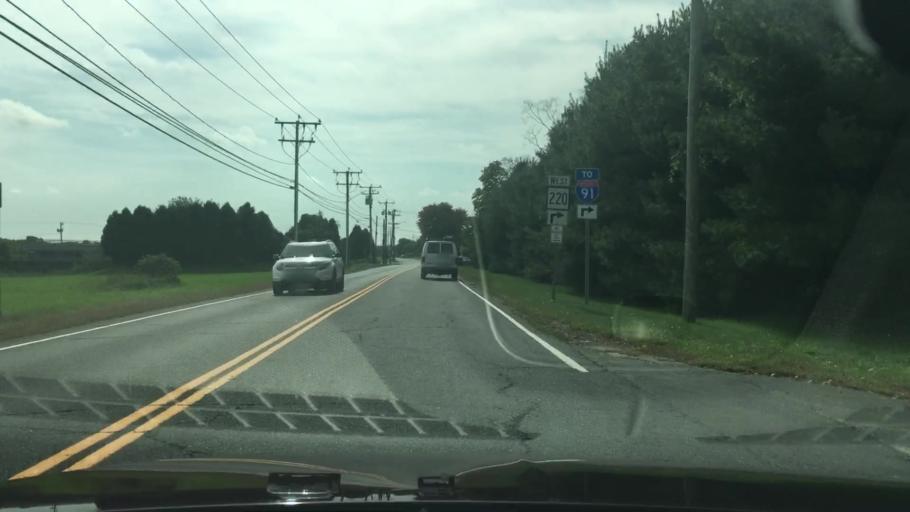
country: US
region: Connecticut
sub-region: Hartford County
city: Hazardville
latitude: 42.0165
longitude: -72.5140
